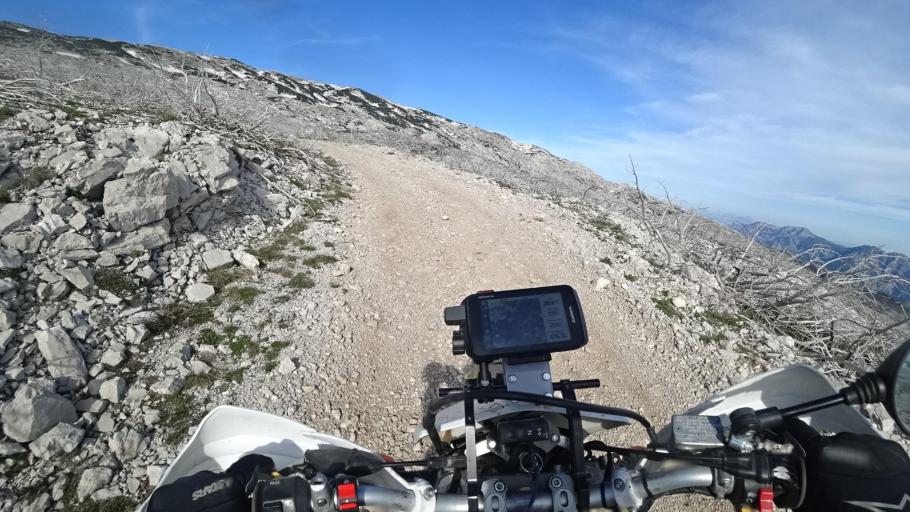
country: BA
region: Federation of Bosnia and Herzegovina
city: Kocerin
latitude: 43.5877
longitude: 17.5375
